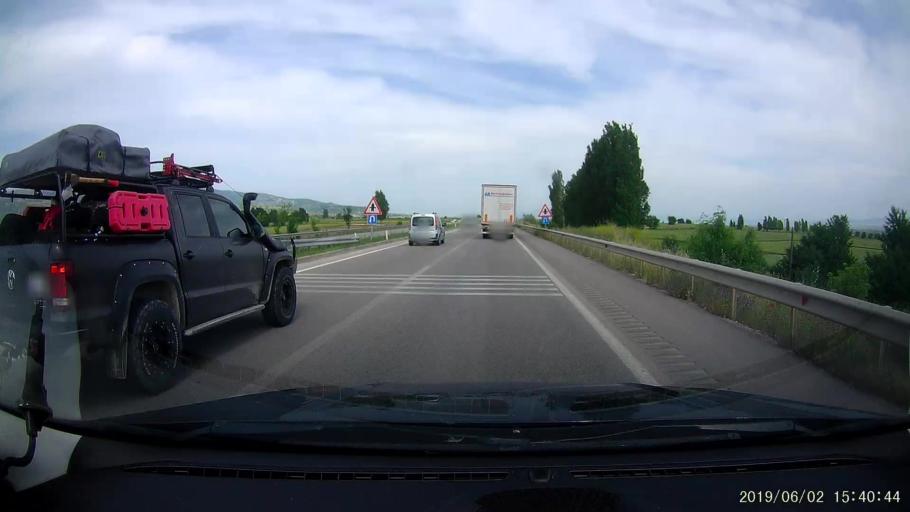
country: TR
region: Amasya
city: Gumushacikoy
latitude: 40.8663
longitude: 35.2862
